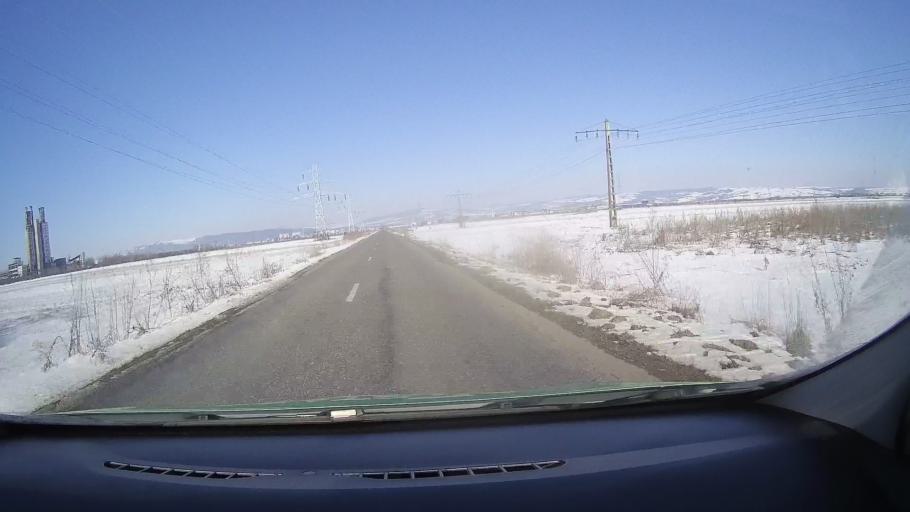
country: RO
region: Brasov
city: Fogarasch
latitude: 45.8110
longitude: 24.9894
